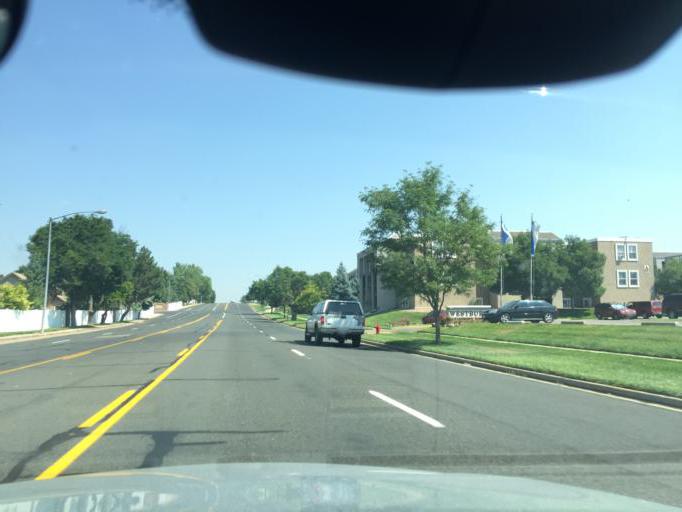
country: US
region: Colorado
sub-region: Adams County
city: Northglenn
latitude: 39.9055
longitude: -105.0061
